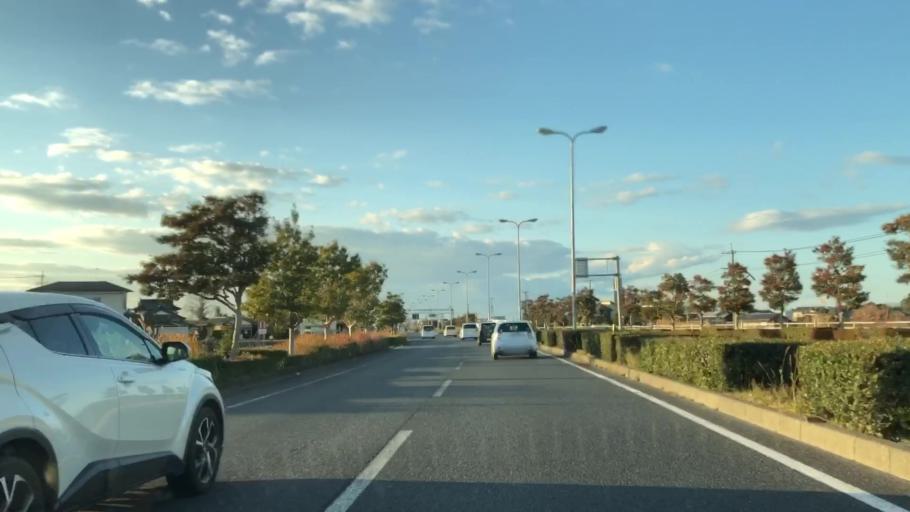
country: JP
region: Fukuoka
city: Nakatsu
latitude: 33.5439
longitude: 131.2867
